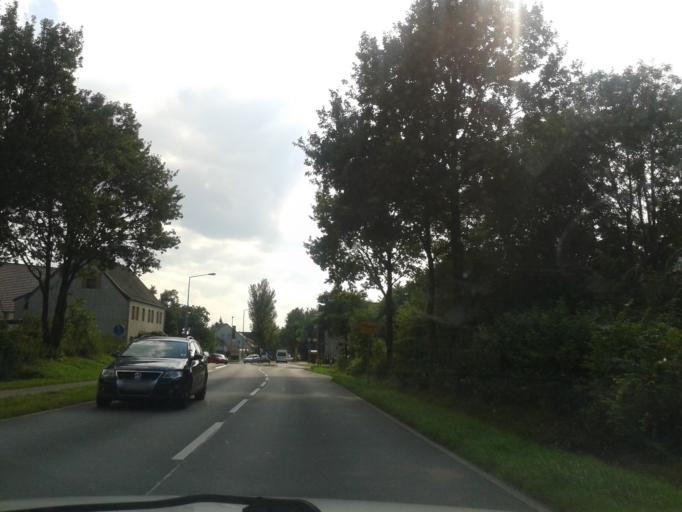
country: DE
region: North Rhine-Westphalia
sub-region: Regierungsbezirk Detmold
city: Schlangen
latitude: 51.8158
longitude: 8.8495
